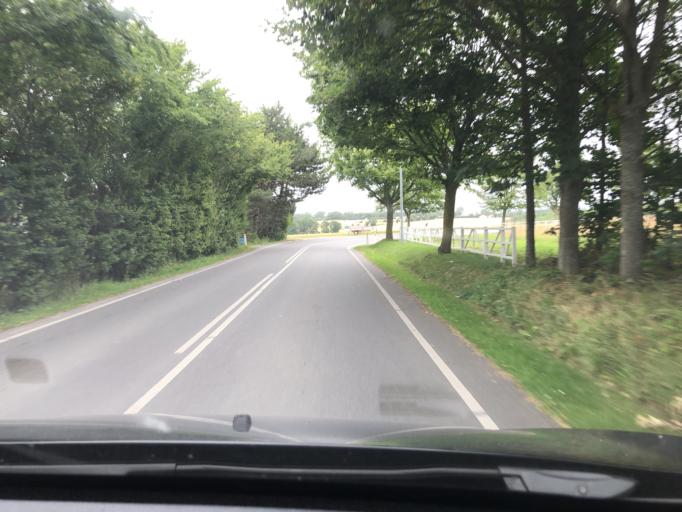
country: DK
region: South Denmark
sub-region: AEro Kommune
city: Marstal
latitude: 54.8544
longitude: 10.4980
